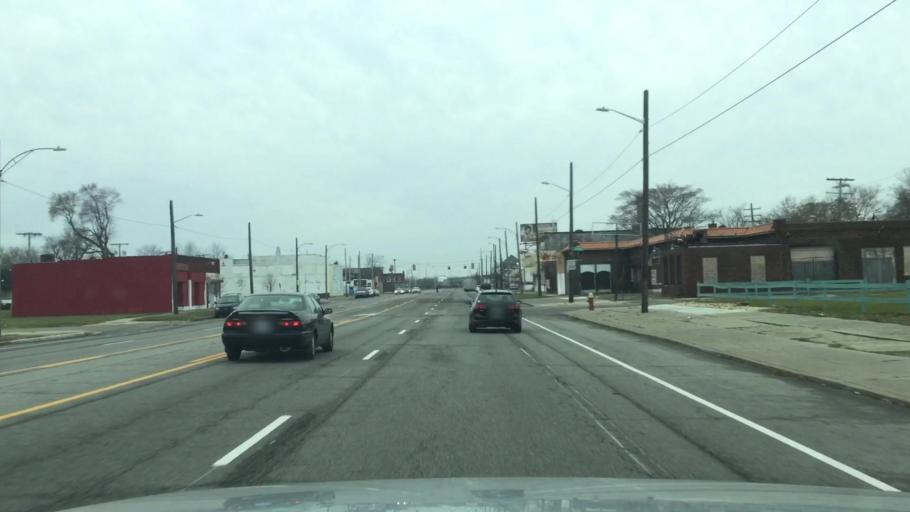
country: US
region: Michigan
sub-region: Wayne County
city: Grosse Pointe Park
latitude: 42.3853
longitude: -82.9592
